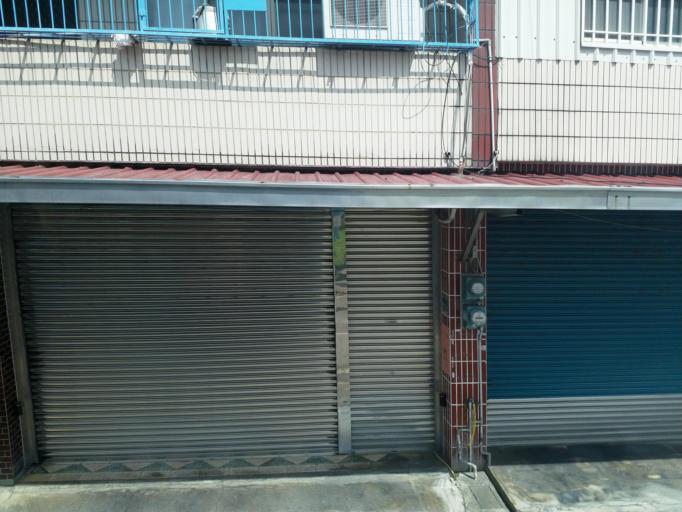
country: TW
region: Taiwan
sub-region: Pingtung
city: Pingtung
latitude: 22.8834
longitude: 120.5567
